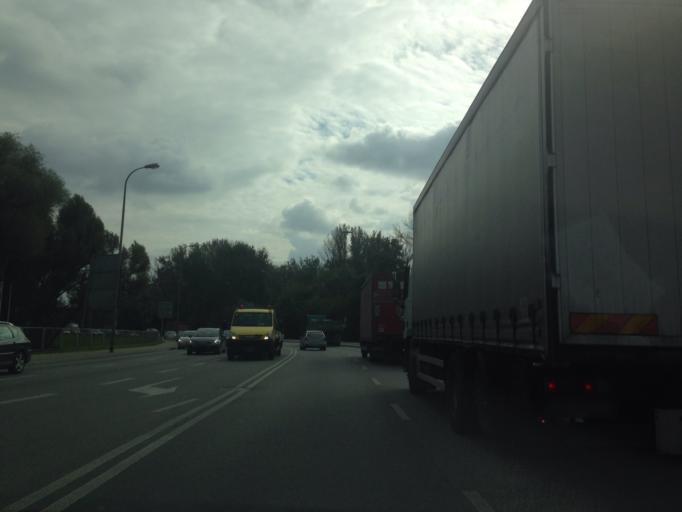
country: PL
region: Masovian Voivodeship
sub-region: Warszawa
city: Praga Polnoc
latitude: 52.2428
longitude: 21.0390
